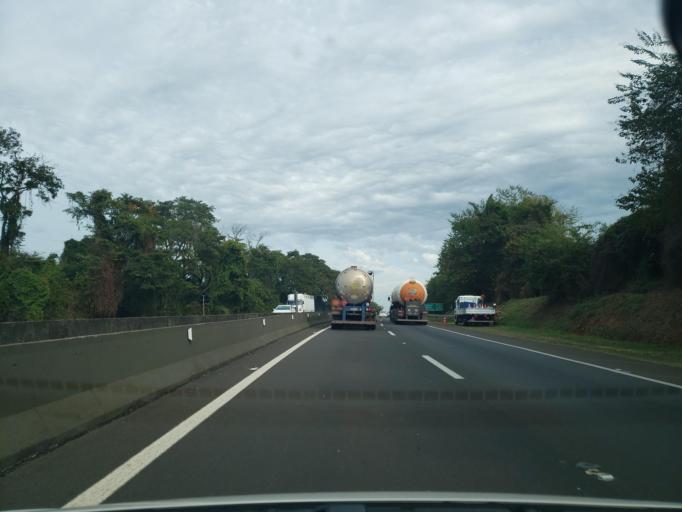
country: BR
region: Sao Paulo
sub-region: Itirapina
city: Itirapina
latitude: -22.2549
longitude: -47.8428
